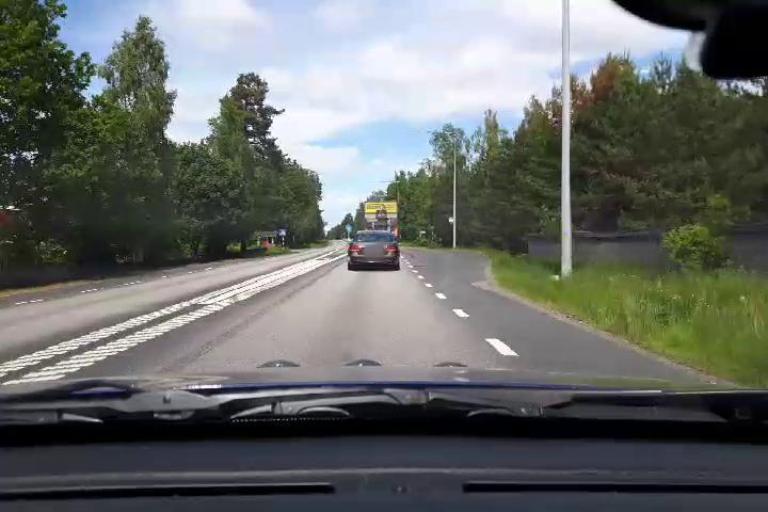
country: SE
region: Uppsala
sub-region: Osthammars Kommun
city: Bjorklinge
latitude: 60.0390
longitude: 17.5505
